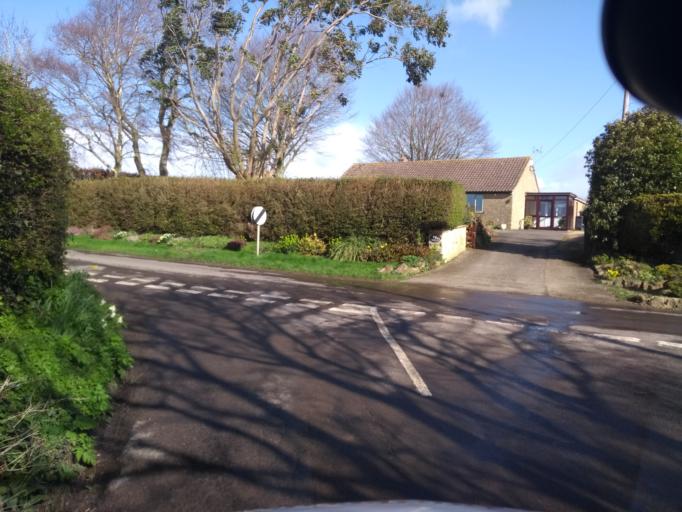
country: GB
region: England
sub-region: Somerset
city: South Petherton
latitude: 50.9679
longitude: -2.8336
